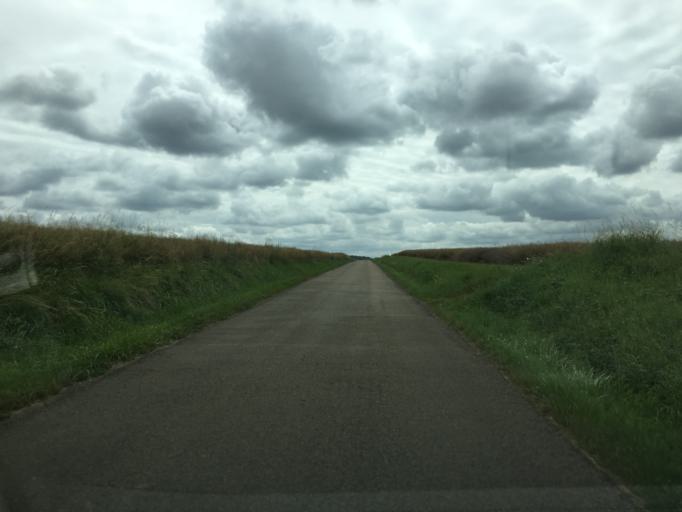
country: FR
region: Bourgogne
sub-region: Departement de l'Yonne
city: Fleury-la-Vallee
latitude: 47.8794
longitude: 3.4274
